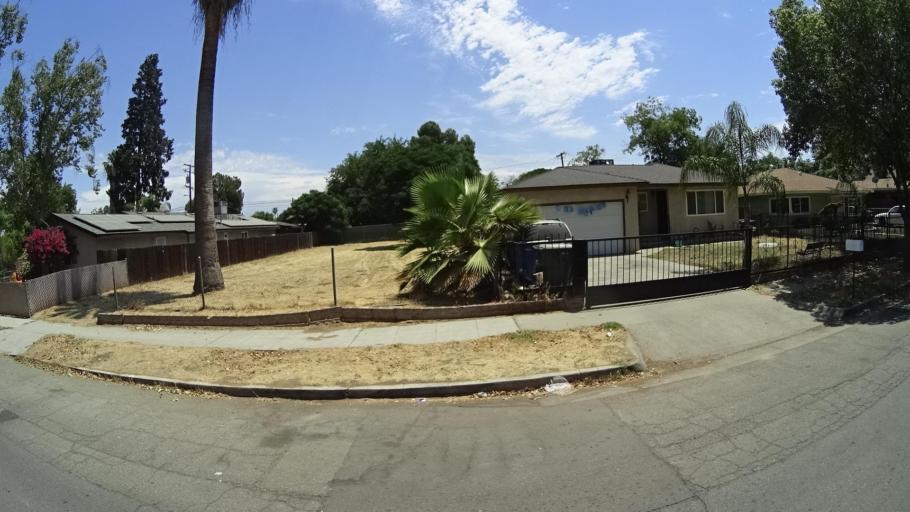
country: US
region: California
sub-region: Fresno County
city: Fresno
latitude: 36.7238
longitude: -119.7681
